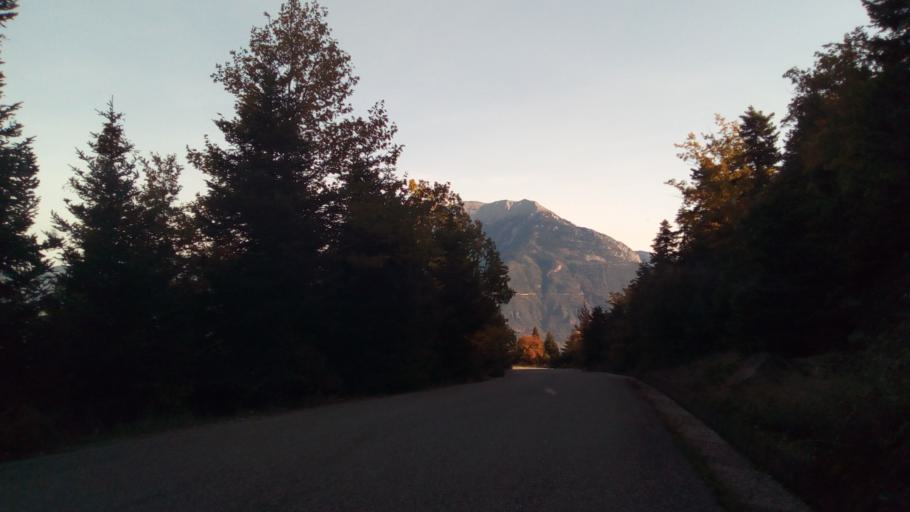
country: GR
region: West Greece
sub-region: Nomos Aitolias kai Akarnanias
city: Thermo
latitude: 38.6458
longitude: 21.8446
